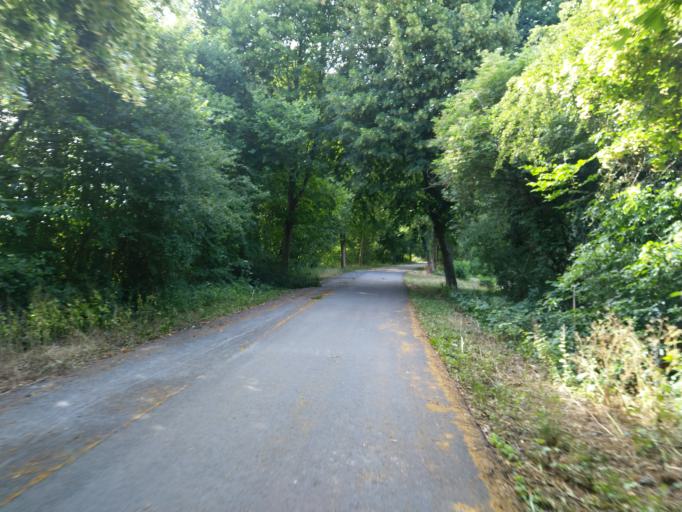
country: BE
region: Wallonia
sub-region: Province du Hainaut
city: Erquelinnes
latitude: 50.3130
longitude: 4.1184
